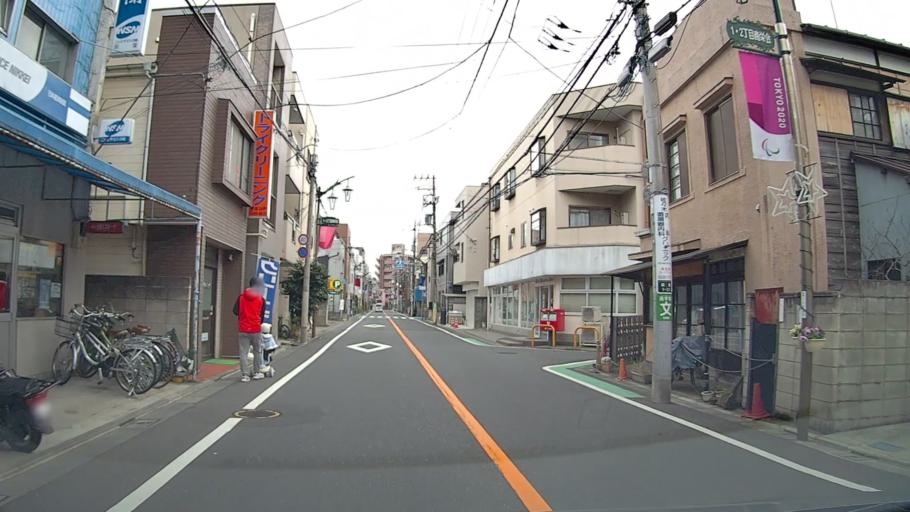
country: JP
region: Tokyo
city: Mitaka-shi
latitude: 35.6934
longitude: 139.6197
